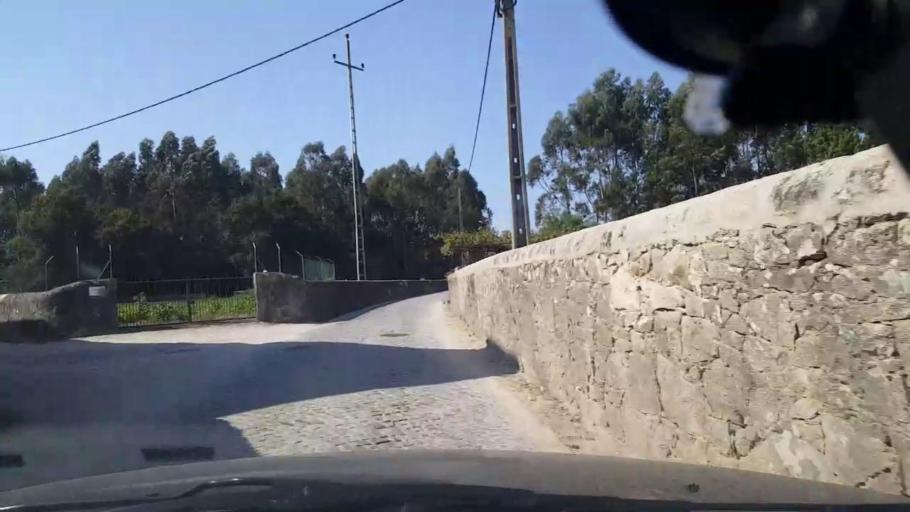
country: PT
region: Porto
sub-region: Povoa de Varzim
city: Pedroso
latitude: 41.3890
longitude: -8.7092
